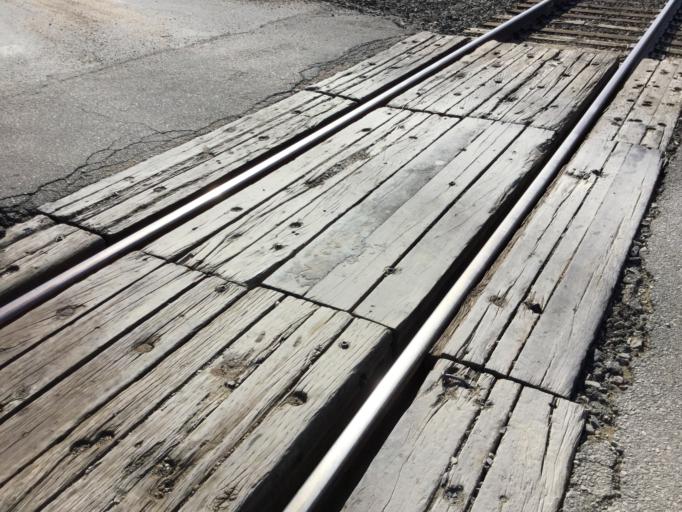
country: US
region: Kansas
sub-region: Dickinson County
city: Solomon
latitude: 38.9022
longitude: -97.4280
